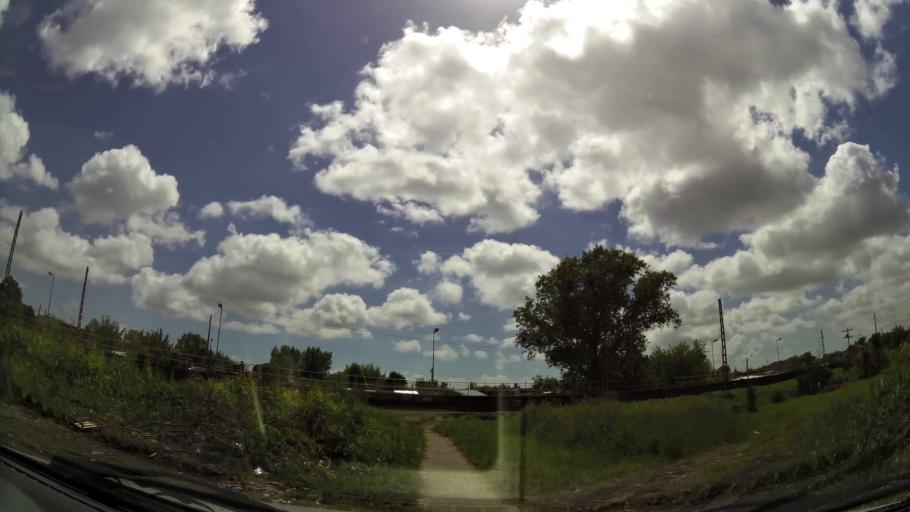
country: AR
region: Buenos Aires
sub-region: Partido de Quilmes
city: Quilmes
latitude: -34.8256
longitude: -58.2124
